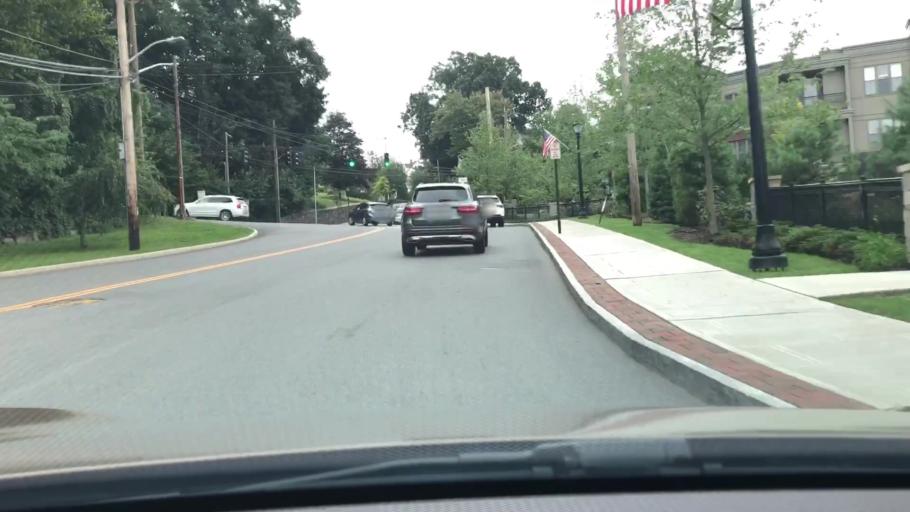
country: US
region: New York
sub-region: Westchester County
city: Tuckahoe
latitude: 40.9488
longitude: -73.8223
